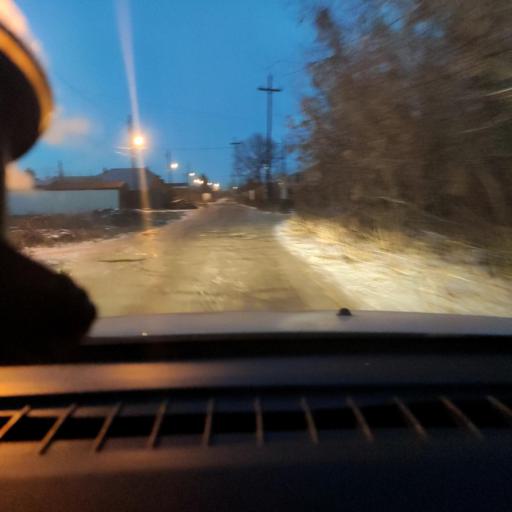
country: RU
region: Samara
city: Smyshlyayevka
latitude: 53.2528
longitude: 50.3551
